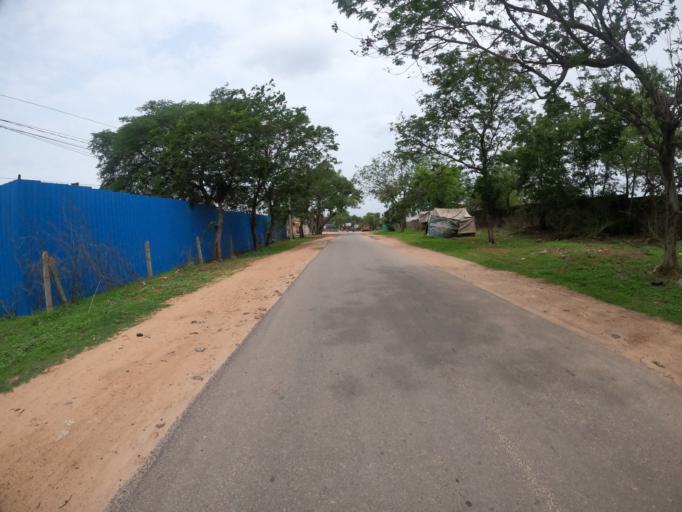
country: IN
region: Telangana
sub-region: Hyderabad
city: Hyderabad
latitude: 17.3424
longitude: 78.3735
